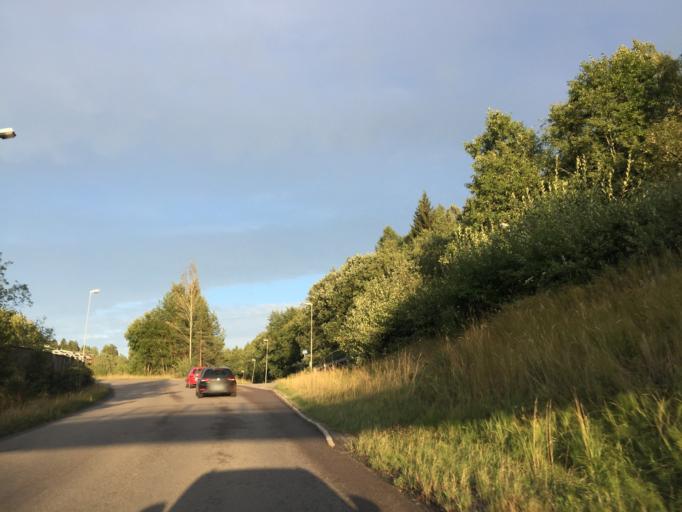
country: NO
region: Akershus
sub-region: Ski
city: Ski
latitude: 59.7613
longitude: 10.8439
